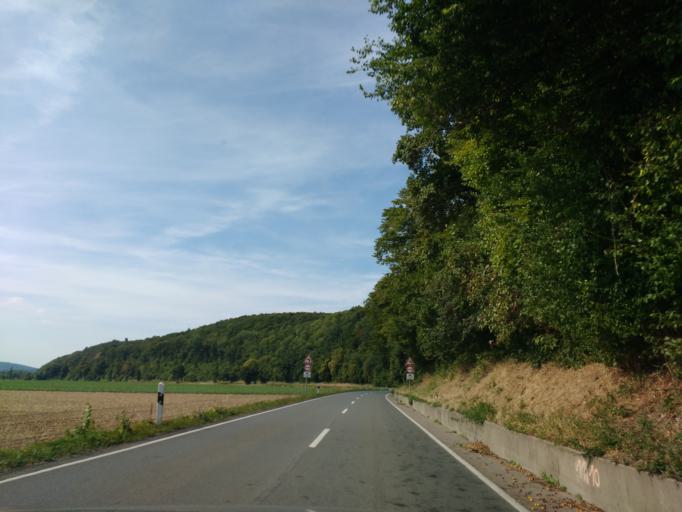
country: DE
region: Lower Saxony
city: Hehlen
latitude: 52.0405
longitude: 9.4204
